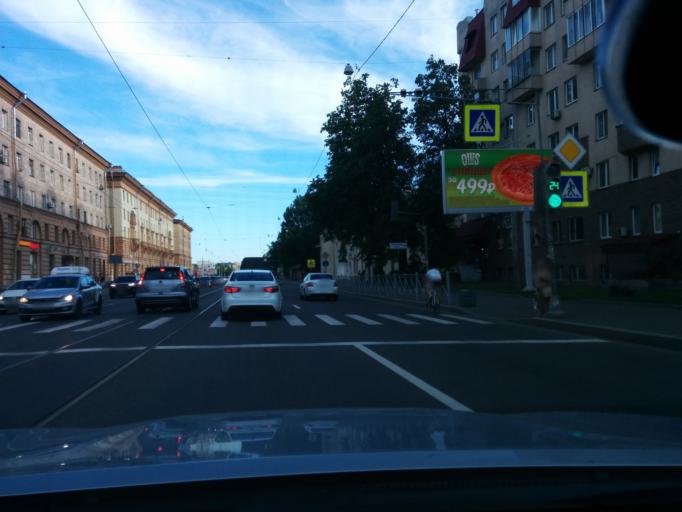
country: RU
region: Leningrad
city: Udel'naya
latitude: 60.0132
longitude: 30.3237
